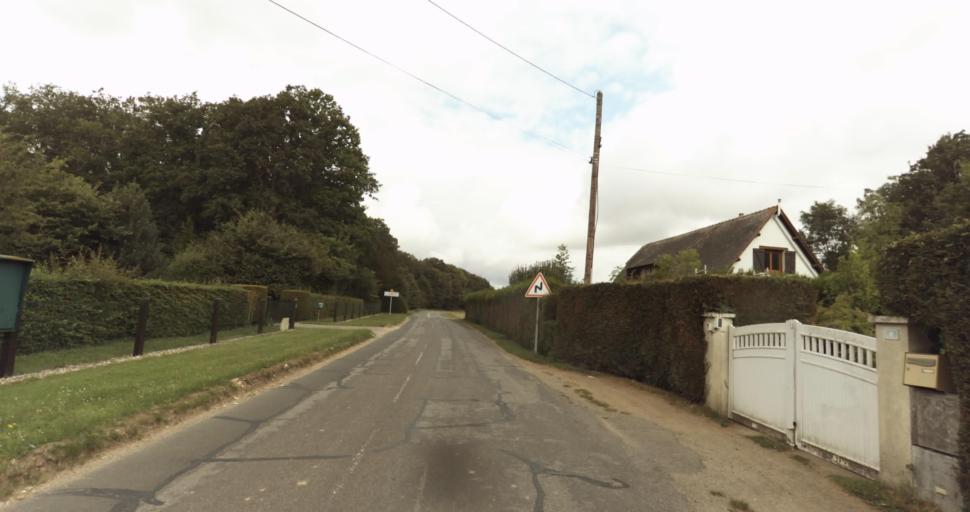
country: FR
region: Haute-Normandie
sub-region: Departement de l'Eure
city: Menilles
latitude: 48.9775
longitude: 1.2802
